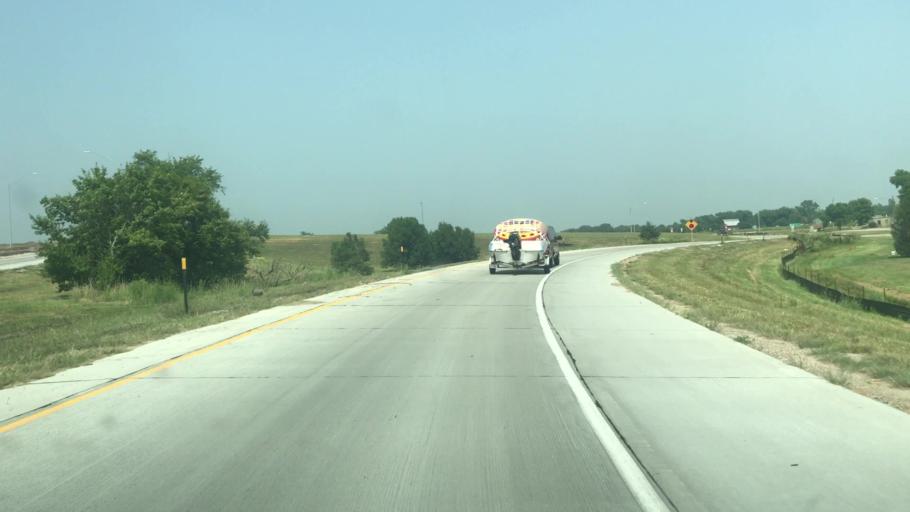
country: US
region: Nebraska
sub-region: Hall County
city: Grand Island
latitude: 40.9504
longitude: -98.3840
